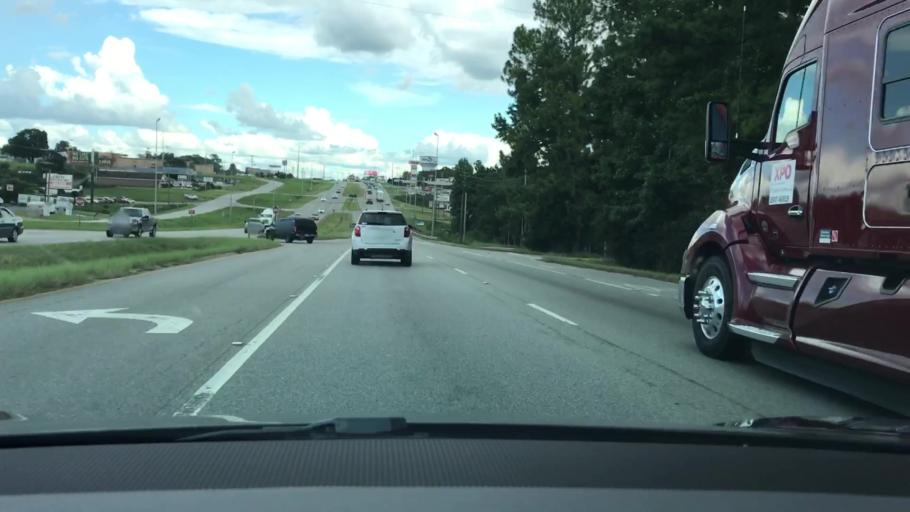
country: US
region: Alabama
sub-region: Pike County
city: Troy
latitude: 31.7885
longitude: -85.9708
